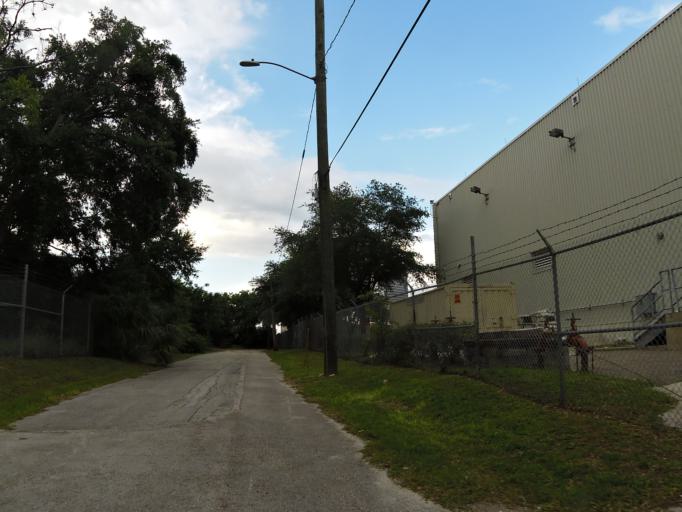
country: US
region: Florida
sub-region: Duval County
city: Jacksonville
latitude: 30.3253
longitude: -81.6702
